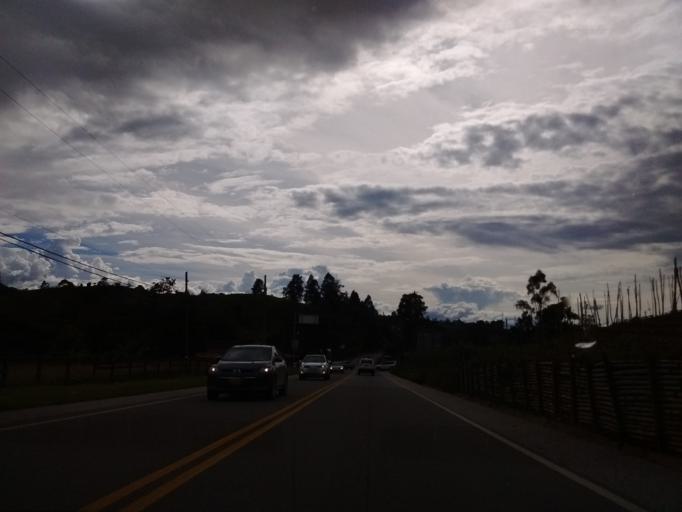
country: CO
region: Antioquia
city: Santuario
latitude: 6.1249
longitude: -75.2450
